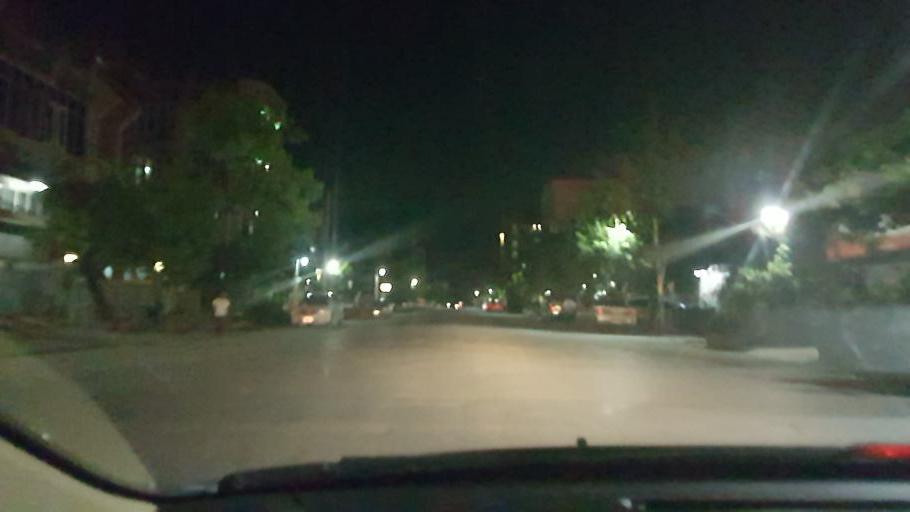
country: MM
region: Mandalay
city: Mandalay
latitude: 21.9813
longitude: 96.0909
